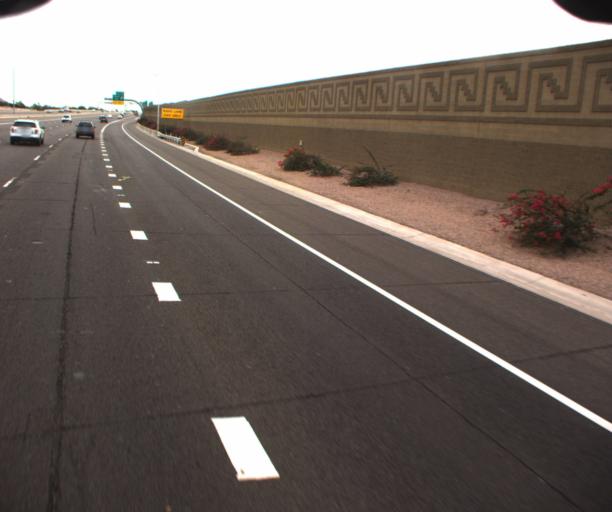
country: US
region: Arizona
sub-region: Maricopa County
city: Phoenix
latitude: 33.4618
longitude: -112.0197
